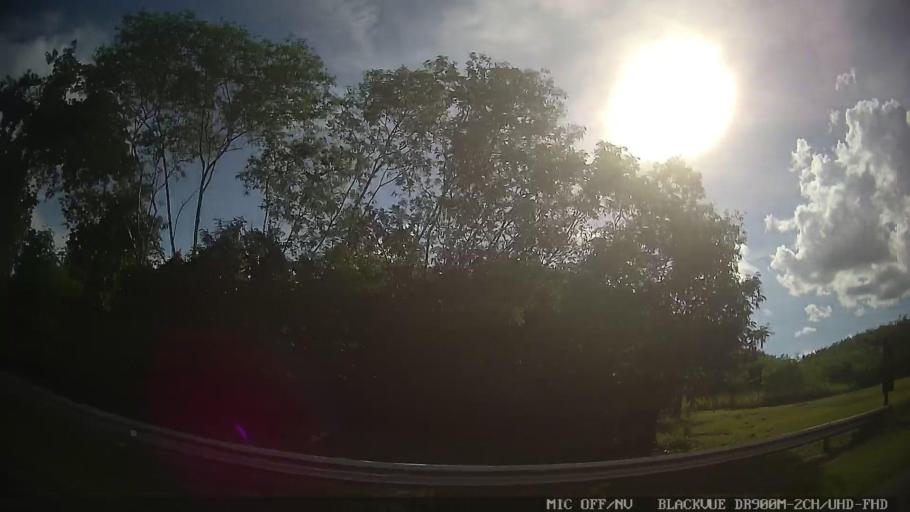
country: BR
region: Sao Paulo
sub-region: Laranjal Paulista
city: Laranjal Paulista
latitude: -23.0468
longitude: -47.8254
